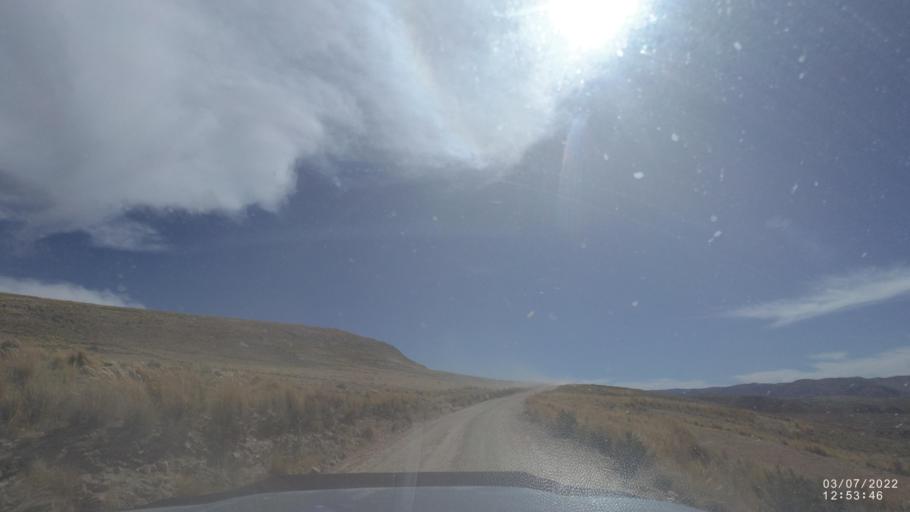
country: BO
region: Cochabamba
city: Irpa Irpa
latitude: -17.7433
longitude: -66.6657
